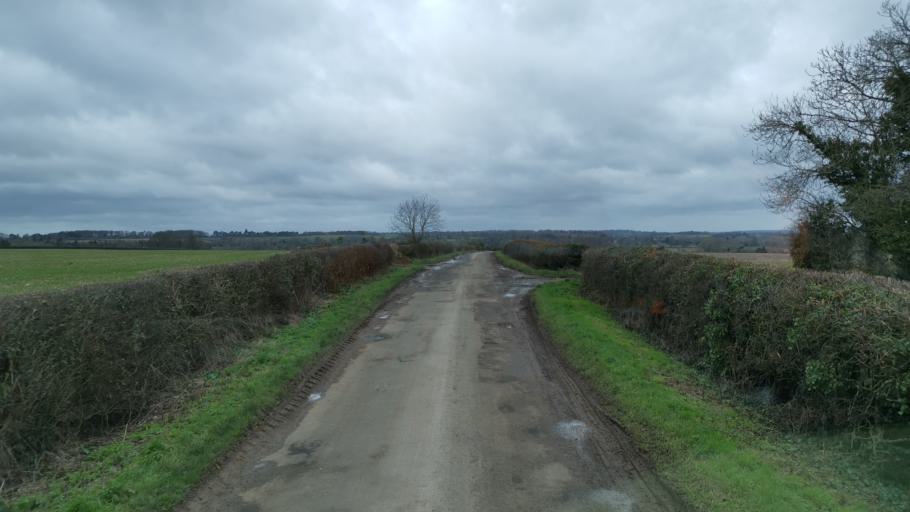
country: GB
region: England
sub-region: Oxfordshire
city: Woodstock
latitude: 51.8949
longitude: -1.3070
